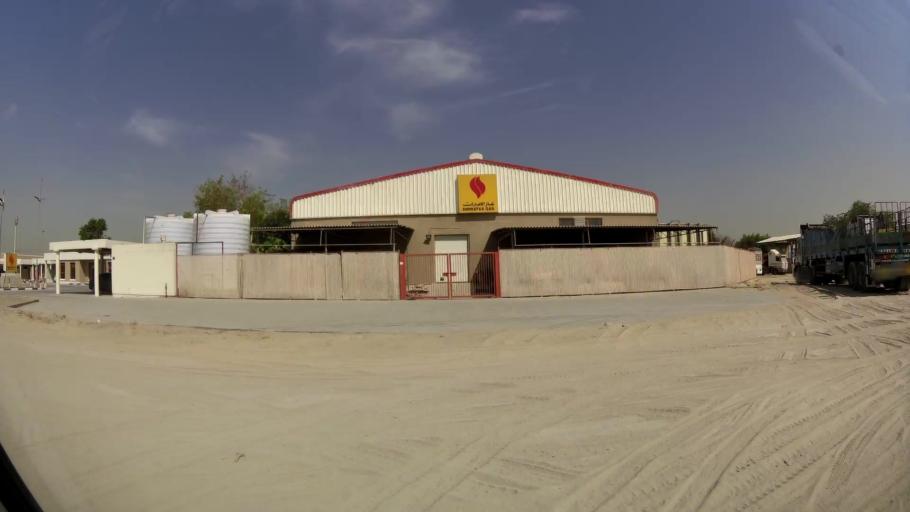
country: AE
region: Ash Shariqah
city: Sharjah
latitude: 25.2783
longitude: 55.3935
